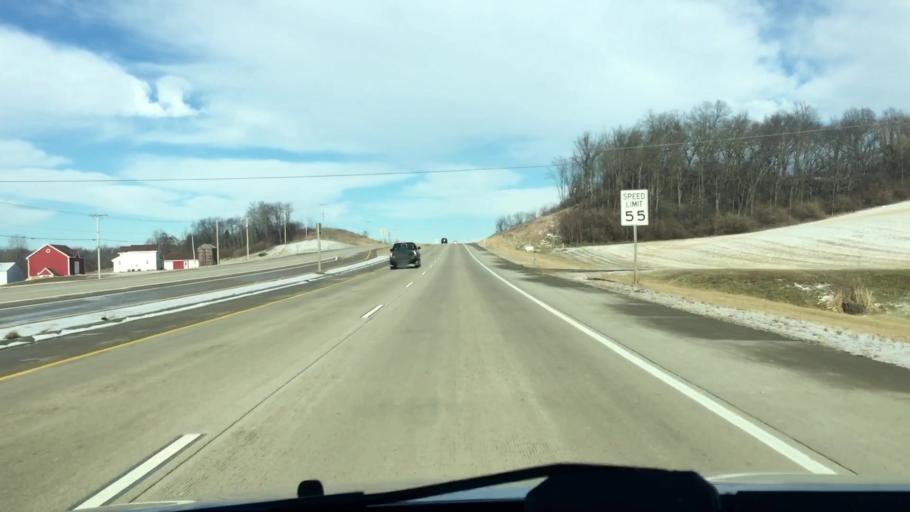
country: US
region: Wisconsin
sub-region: Waukesha County
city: Mukwonago
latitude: 42.9045
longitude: -88.3453
